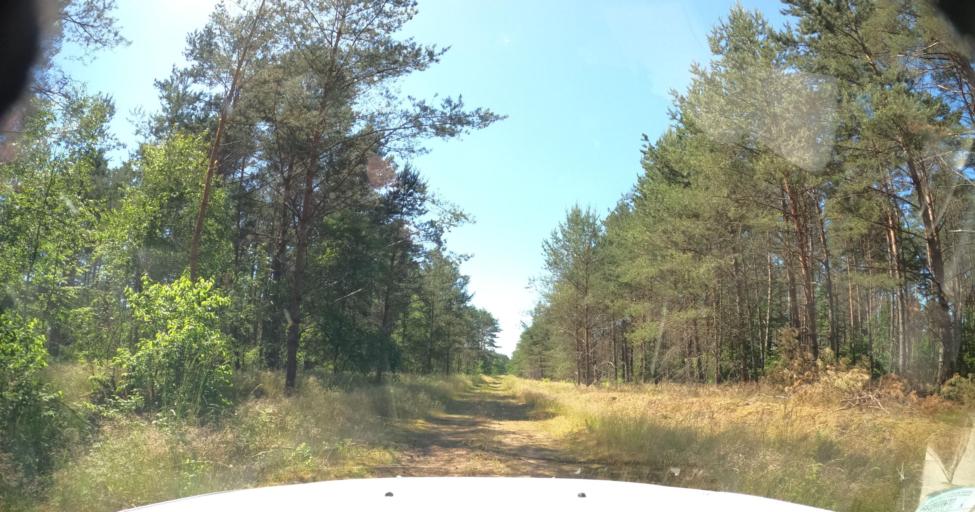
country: PL
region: West Pomeranian Voivodeship
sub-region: Powiat szczecinecki
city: Lubowo
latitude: 53.5880
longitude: 16.4561
